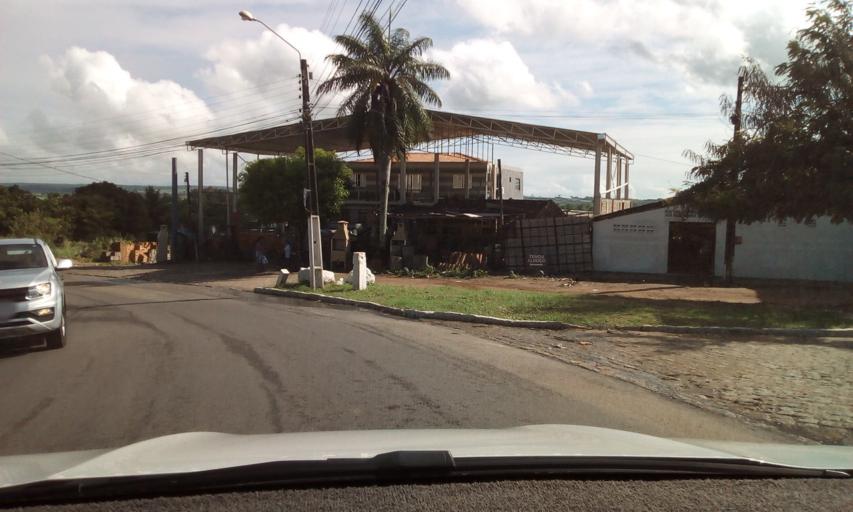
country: BR
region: Paraiba
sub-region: Santa Rita
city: Santa Rita
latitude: -7.1240
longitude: -34.9678
